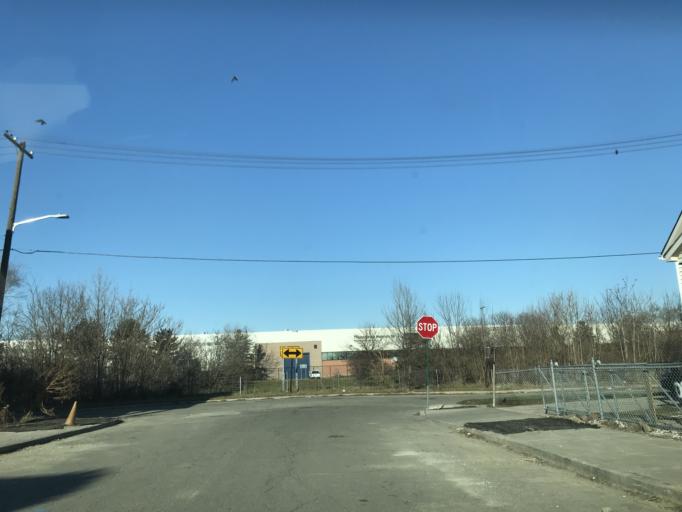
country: US
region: Michigan
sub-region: Wayne County
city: Dearborn
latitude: 42.3384
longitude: -83.1207
